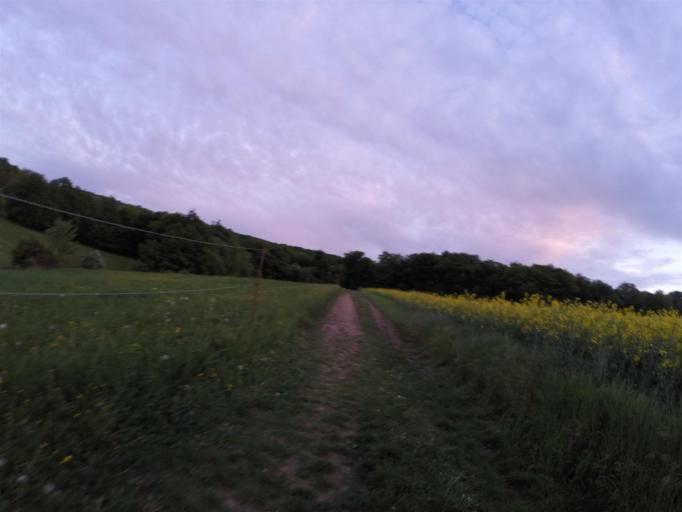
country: DE
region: Thuringia
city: Grosslobichau
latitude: 50.9262
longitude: 11.6619
